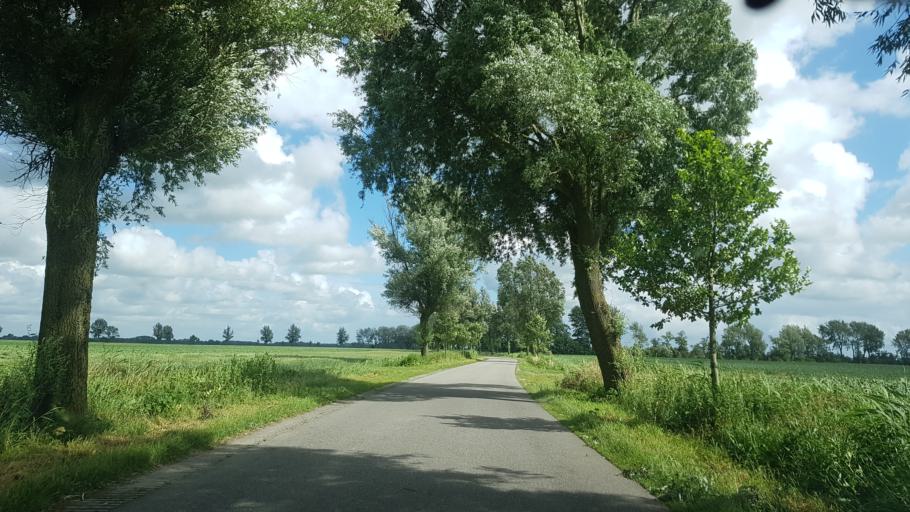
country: NL
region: Groningen
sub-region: Gemeente Winsum
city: Winsum
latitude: 53.3981
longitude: 6.4666
